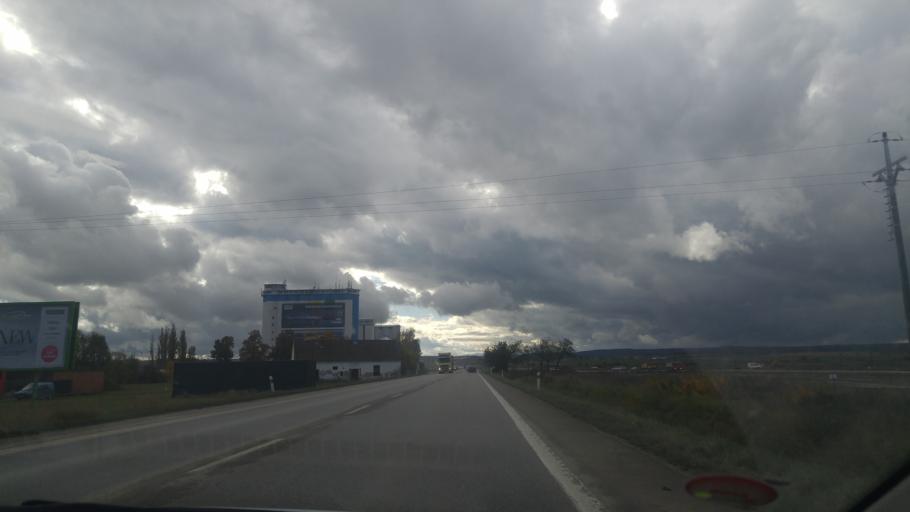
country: CZ
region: Jihocesky
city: Dolni Bukovsko
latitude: 49.1488
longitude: 14.6282
